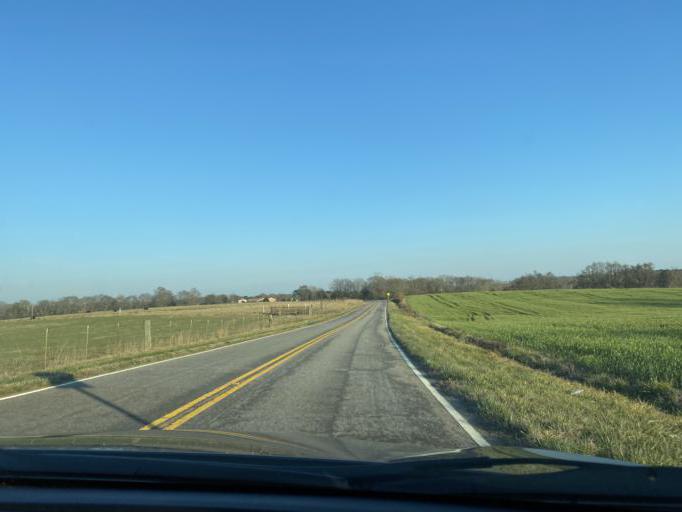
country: US
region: South Carolina
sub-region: Cherokee County
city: Gaffney
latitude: 35.1092
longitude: -81.6655
